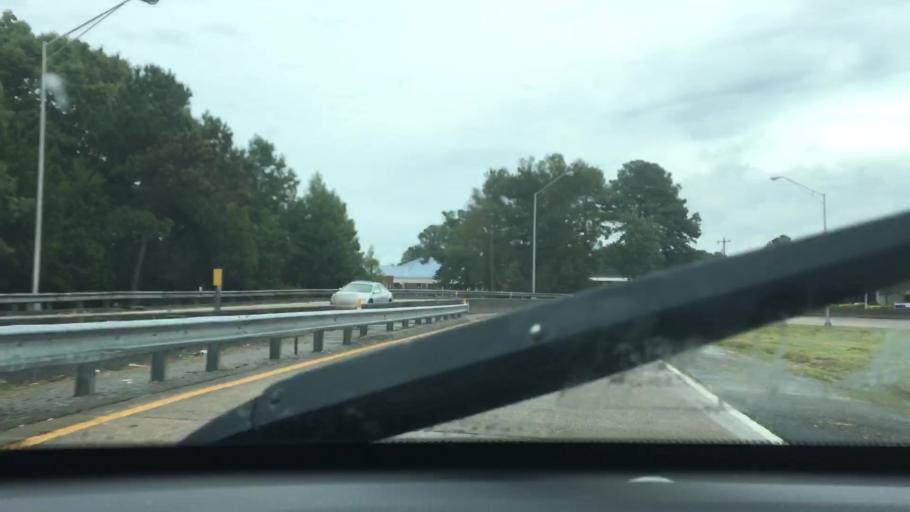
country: US
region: Virginia
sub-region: City of Virginia Beach
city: Virginia Beach
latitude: 36.8370
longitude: -76.0671
